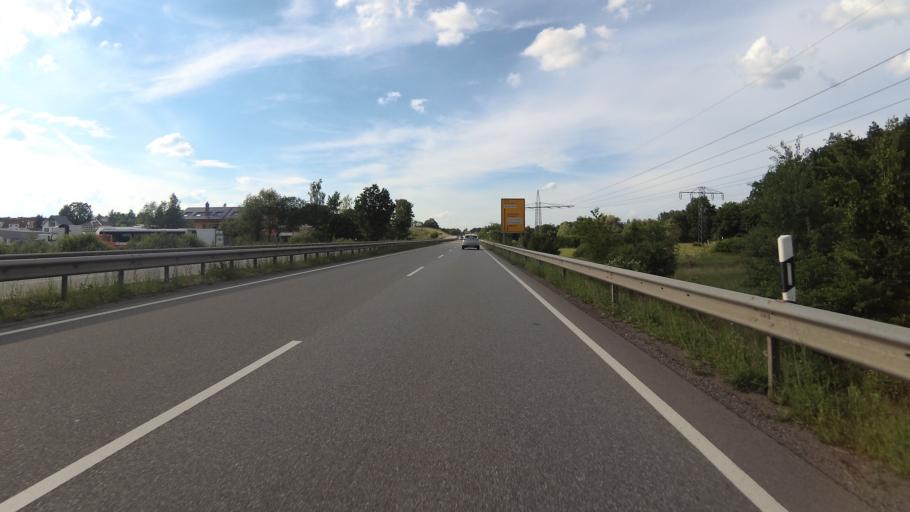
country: DE
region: Rheinland-Pfalz
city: Katzweiler
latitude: 49.4640
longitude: 7.7010
